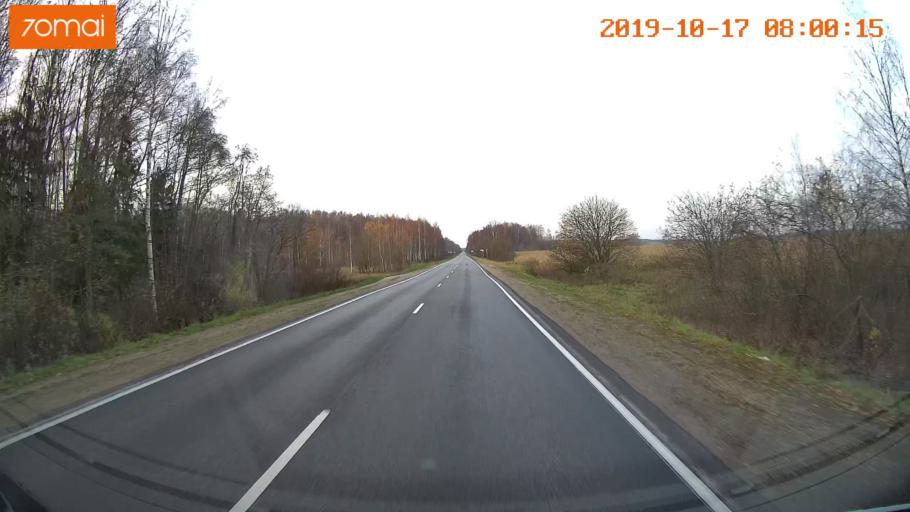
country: RU
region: Vladimir
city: Bavleny
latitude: 56.3853
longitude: 39.5219
